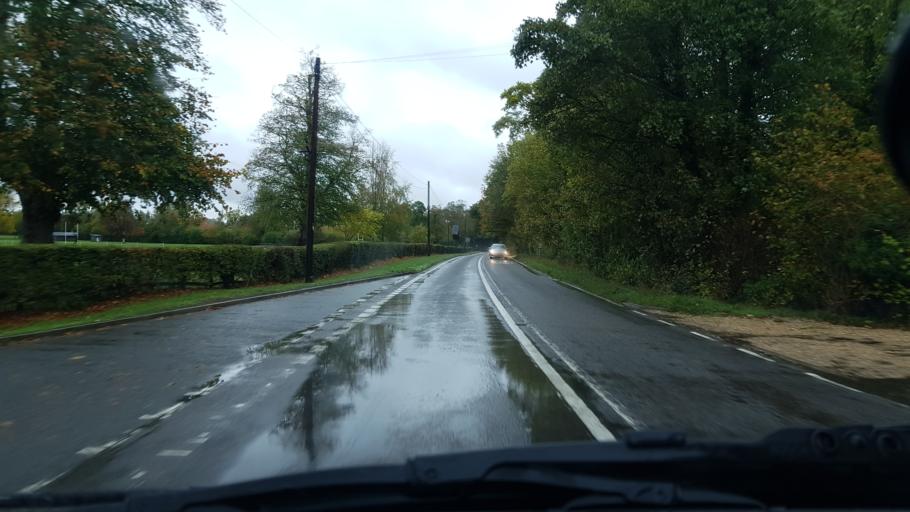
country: GB
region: England
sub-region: Oxfordshire
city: Ducklington
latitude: 51.7561
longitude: -1.4610
